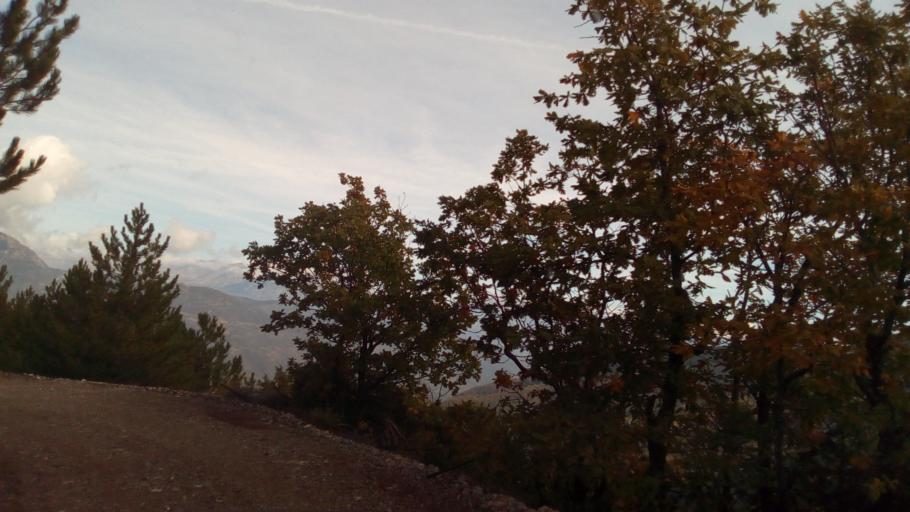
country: GR
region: West Greece
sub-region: Nomos Achaias
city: Kamarai
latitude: 38.4776
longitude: 22.0228
